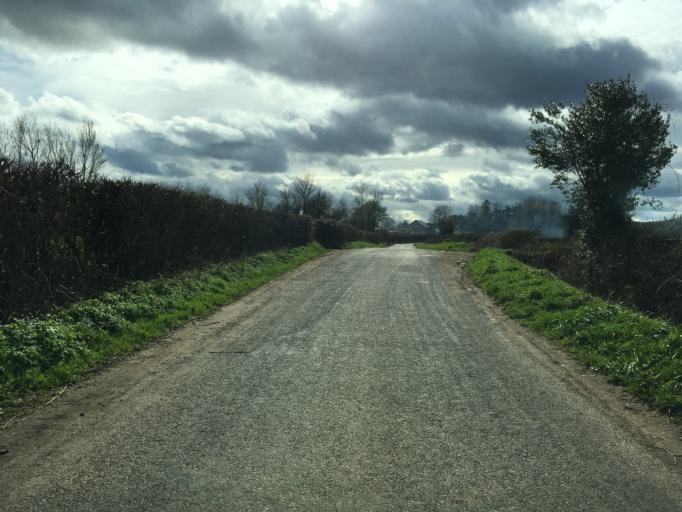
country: GB
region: England
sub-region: Gloucestershire
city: Mitcheldean
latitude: 51.8304
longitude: -2.3999
